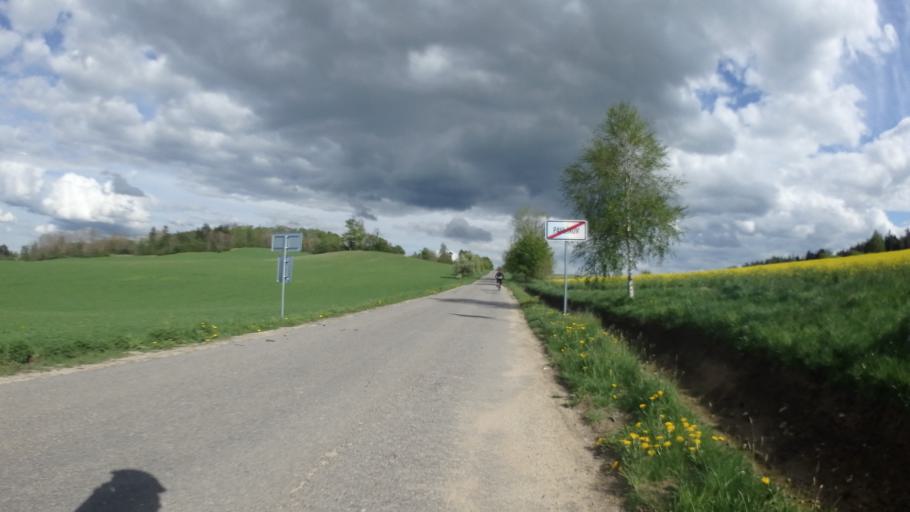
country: CZ
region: Vysocina
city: Merin
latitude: 49.3455
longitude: 15.8821
